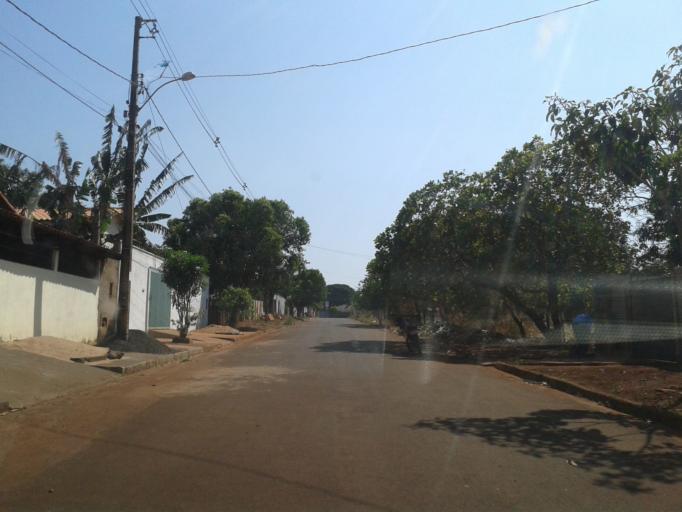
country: BR
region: Minas Gerais
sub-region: Ituiutaba
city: Ituiutaba
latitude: -18.9598
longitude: -49.4828
